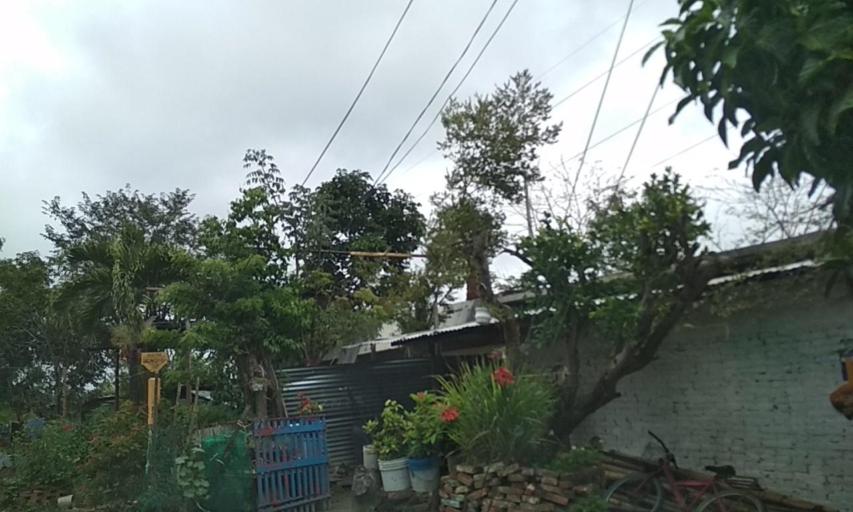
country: MX
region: Veracruz
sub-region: Papantla
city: El Chote
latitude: 20.3744
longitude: -97.3326
